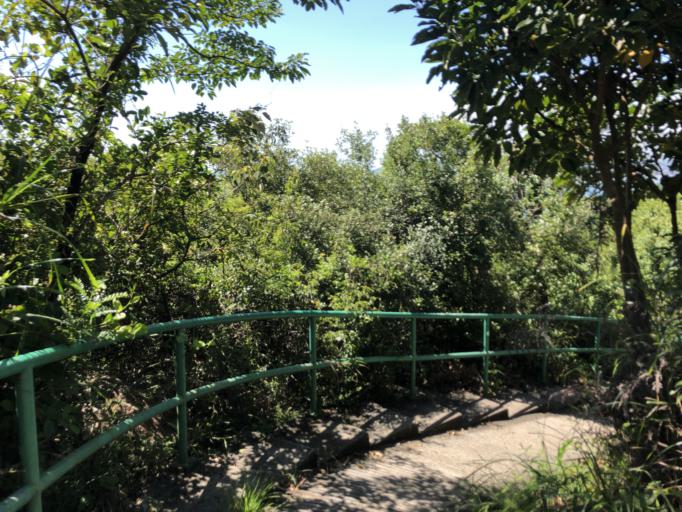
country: HK
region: Tuen Mun
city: Tuen Mun
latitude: 22.2858
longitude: 113.9818
